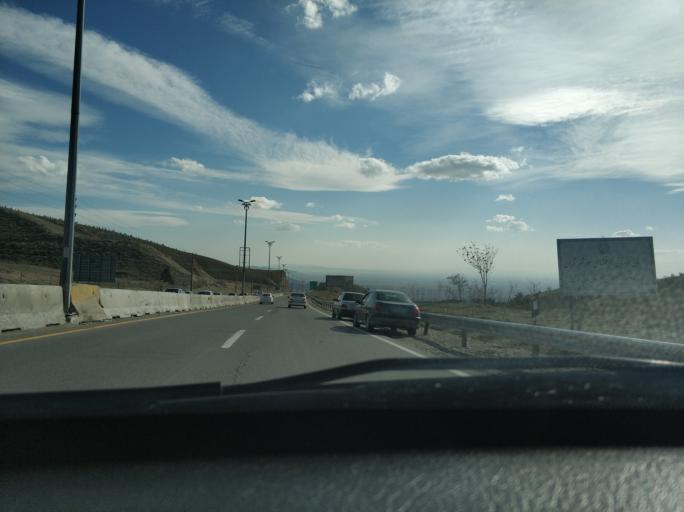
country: IR
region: Tehran
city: Tajrish
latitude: 35.7945
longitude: 51.5705
